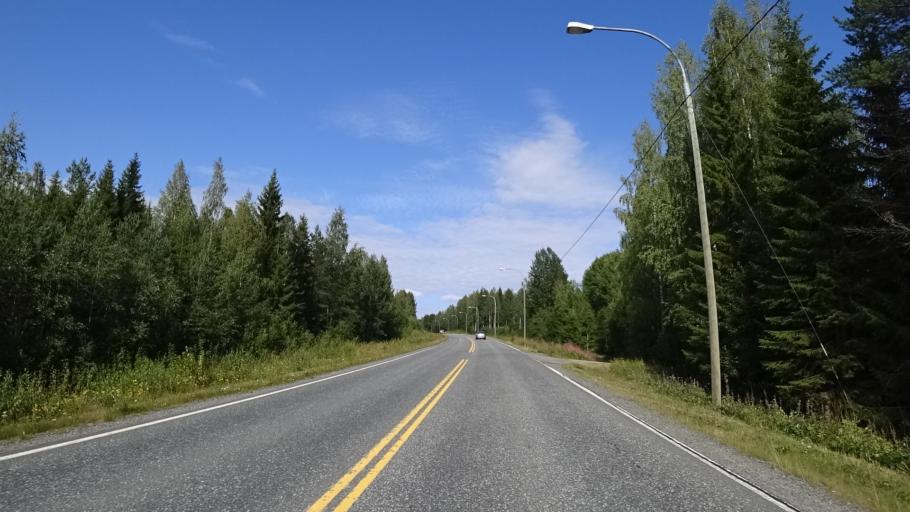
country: FI
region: North Karelia
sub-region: Joensuu
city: Eno
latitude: 62.7800
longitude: 30.0706
